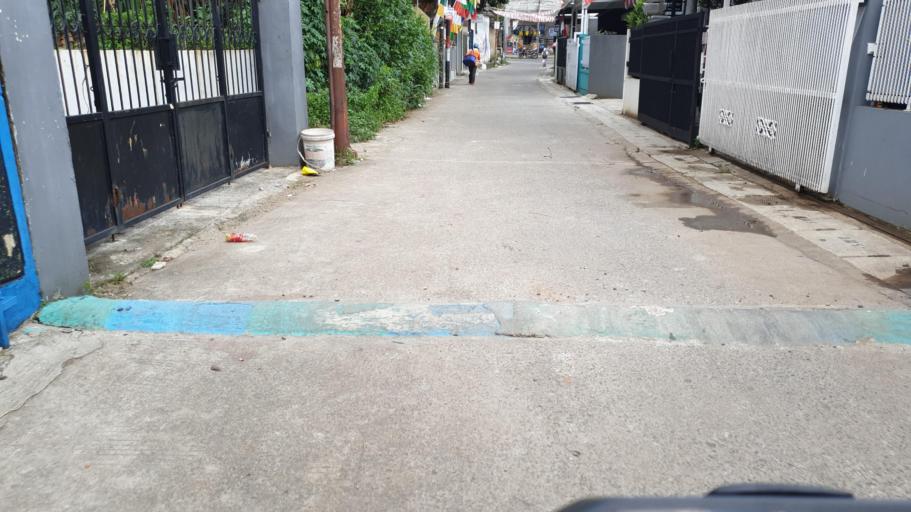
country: ID
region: West Java
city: Depok
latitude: -6.3661
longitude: 106.8452
